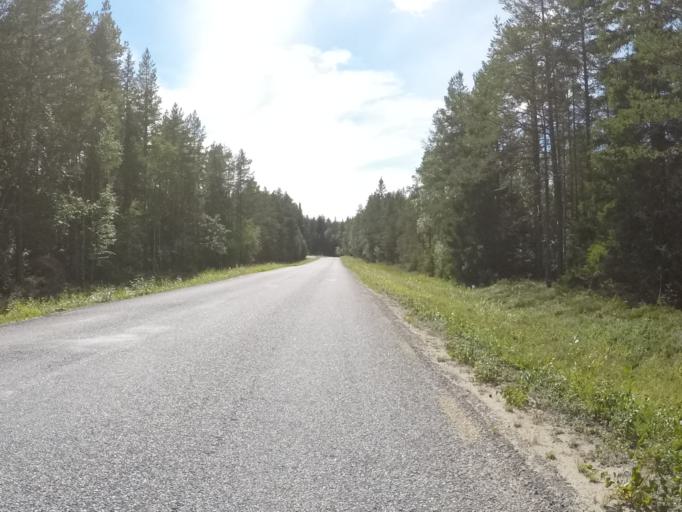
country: SE
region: Vaesterbotten
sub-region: Robertsfors Kommun
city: Robertsfors
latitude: 63.9828
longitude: 20.8115
